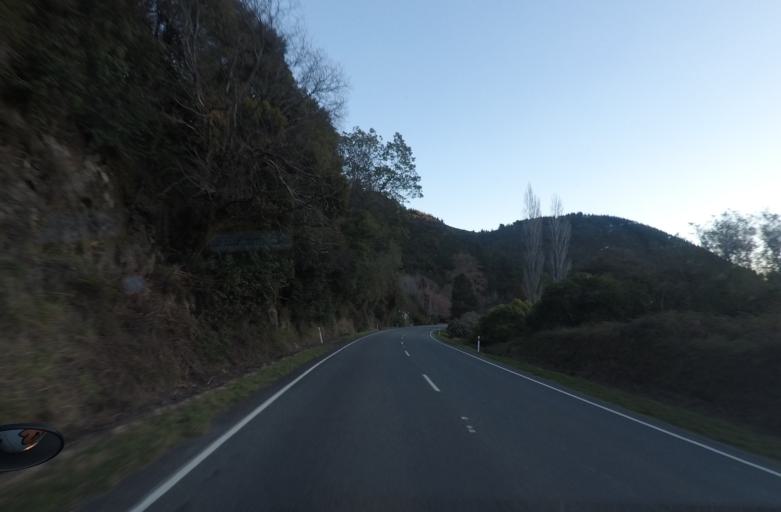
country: NZ
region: Marlborough
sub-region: Marlborough District
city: Picton
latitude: -41.2740
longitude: 173.7442
